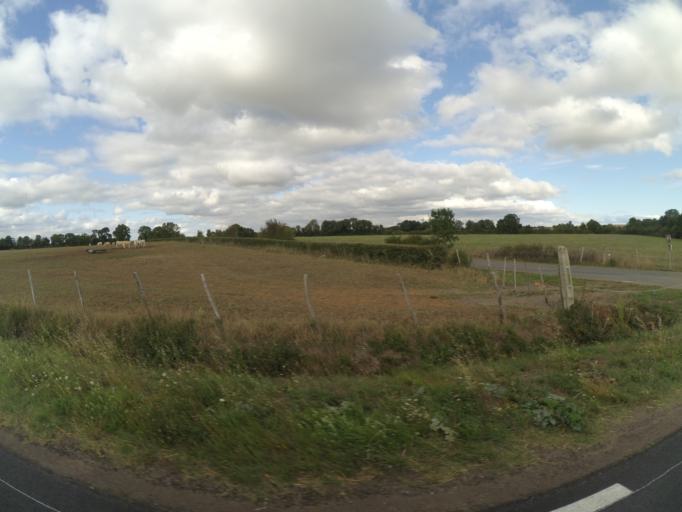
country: FR
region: Pays de la Loire
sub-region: Departement de la Vendee
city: Angles
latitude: 46.4399
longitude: -1.4054
